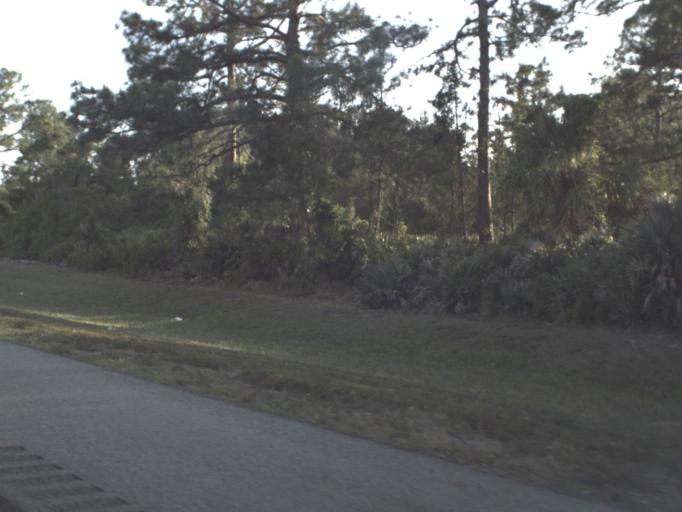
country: US
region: Florida
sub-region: Brevard County
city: Titusville
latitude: 28.5891
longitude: -80.8515
